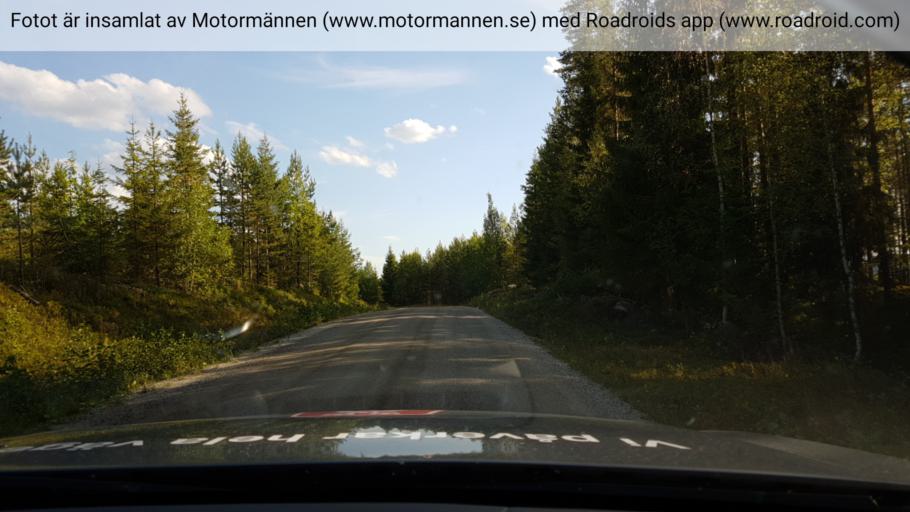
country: SE
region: Vaesternorrland
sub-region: Solleftea Kommun
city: As
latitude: 63.7341
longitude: 16.2386
